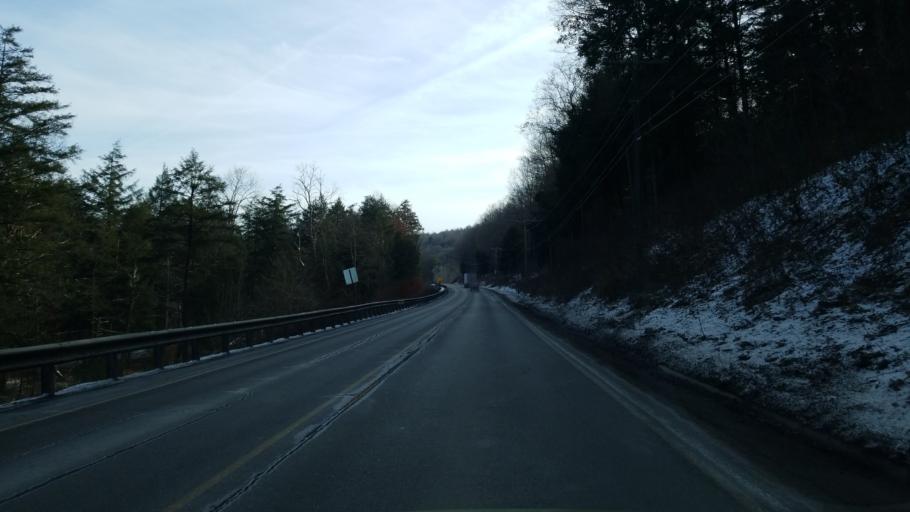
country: US
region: Pennsylvania
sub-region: Clearfield County
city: Treasure Lake
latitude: 41.2037
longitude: -78.5673
